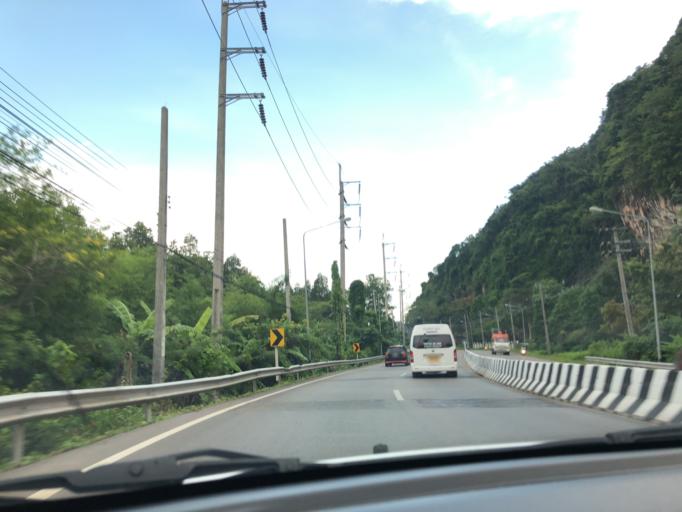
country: TH
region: Krabi
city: Krabi
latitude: 8.0844
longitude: 98.8741
